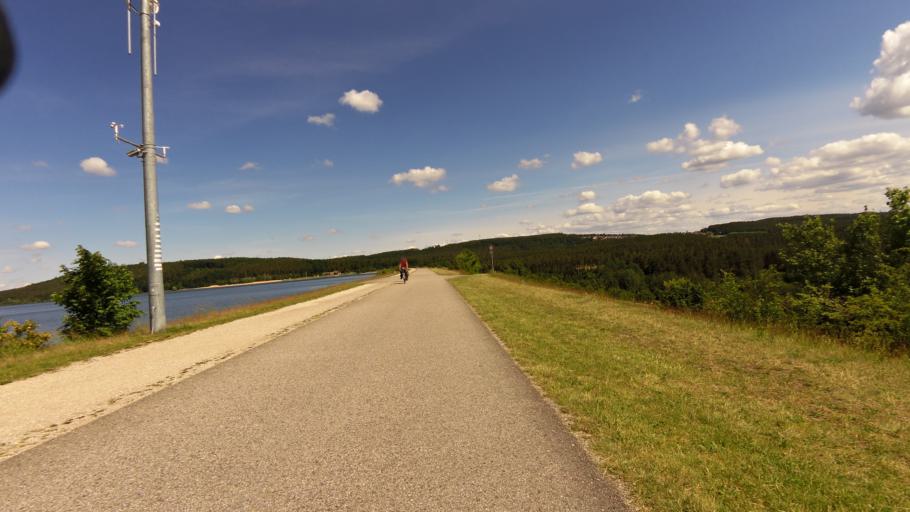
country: DE
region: Bavaria
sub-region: Regierungsbezirk Mittelfranken
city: Pleinfeld
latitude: 49.1236
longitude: 10.9645
